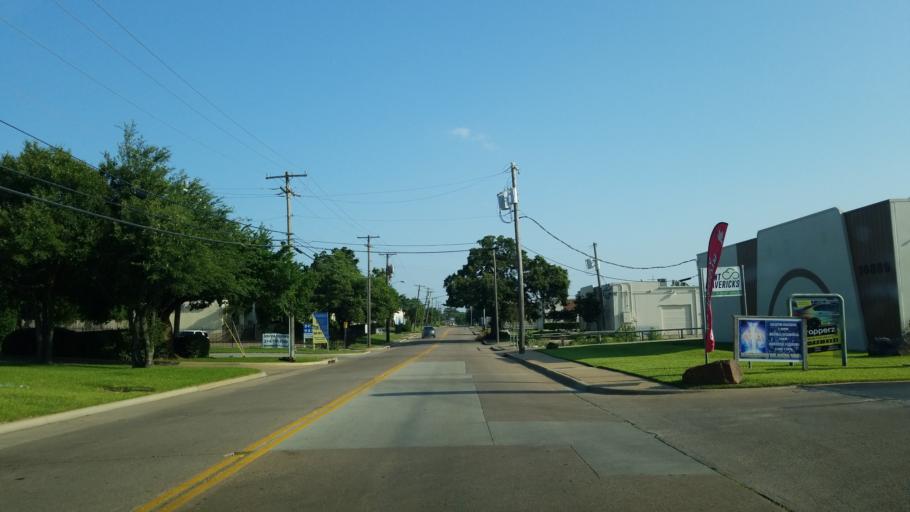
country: US
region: Texas
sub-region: Dallas County
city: Farmers Branch
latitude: 32.8786
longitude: -96.8903
